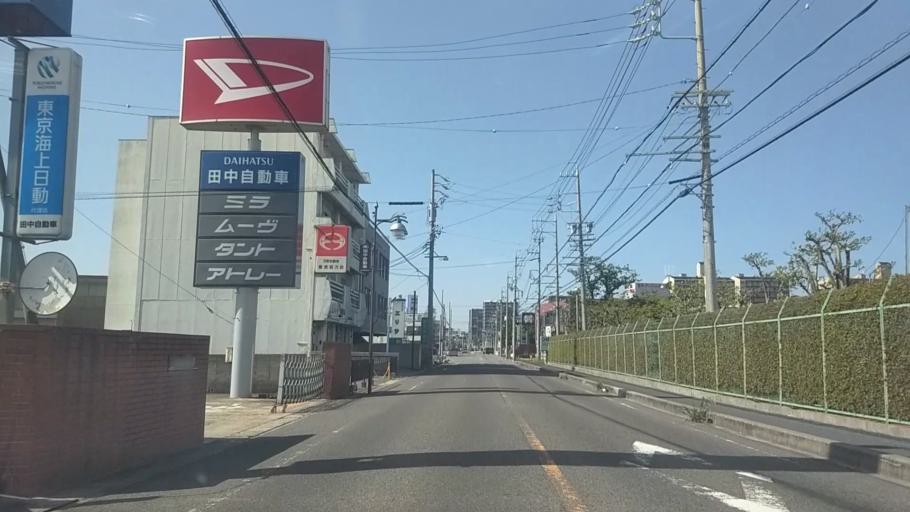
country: JP
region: Aichi
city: Anjo
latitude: 34.9794
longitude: 137.0845
